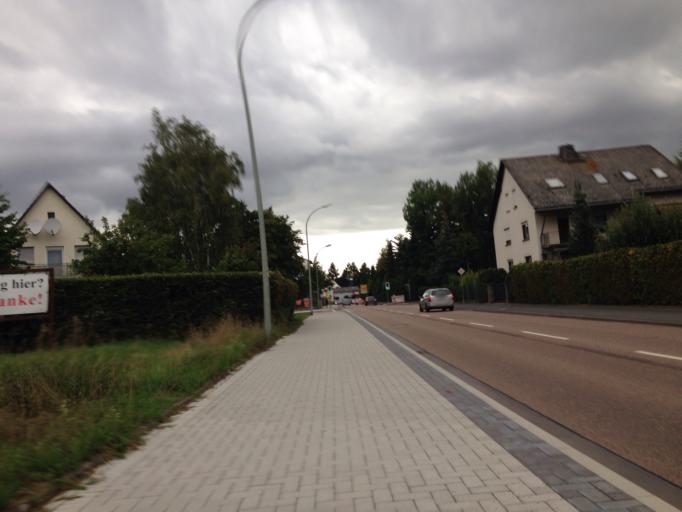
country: DE
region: Hesse
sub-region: Regierungsbezirk Giessen
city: Limburg an der Lahn
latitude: 50.3793
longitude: 8.0719
